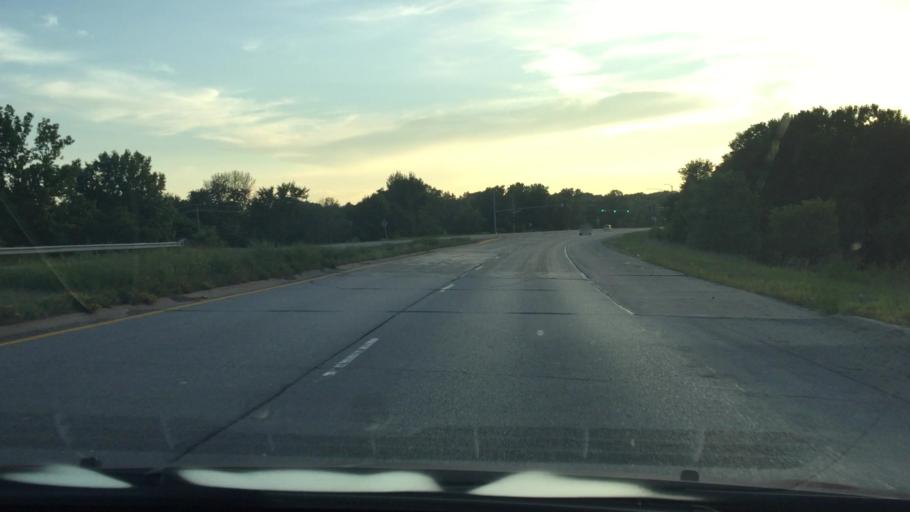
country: US
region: Iowa
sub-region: Muscatine County
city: Muscatine
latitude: 41.4520
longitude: -91.0393
